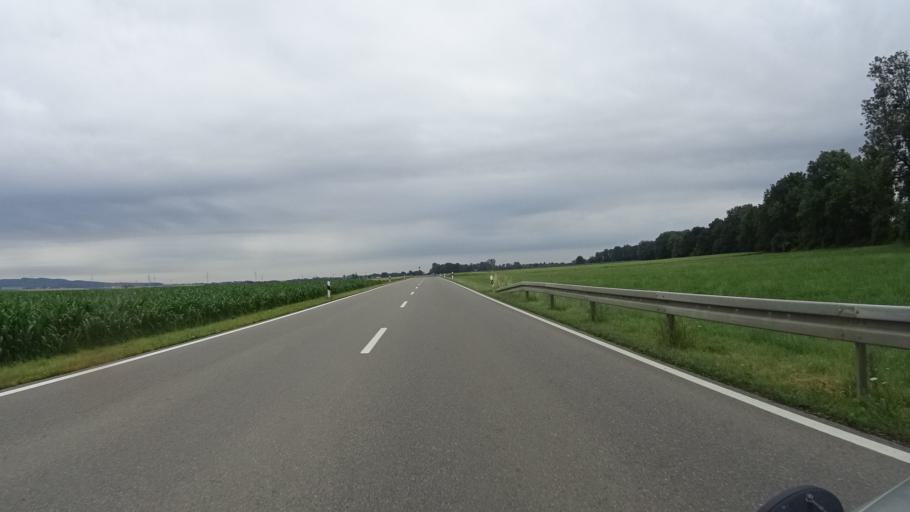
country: DE
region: Bavaria
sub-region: Swabia
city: Fellheim
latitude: 48.0636
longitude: 10.1530
